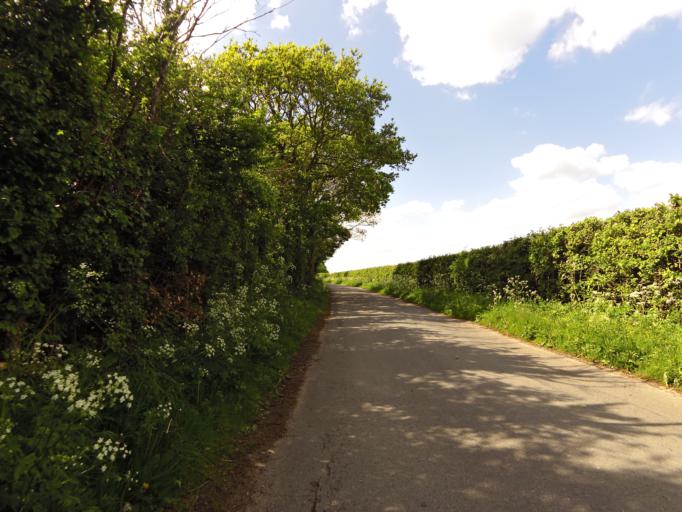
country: GB
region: England
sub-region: Suffolk
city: Wrentham
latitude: 52.4456
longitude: 1.6493
